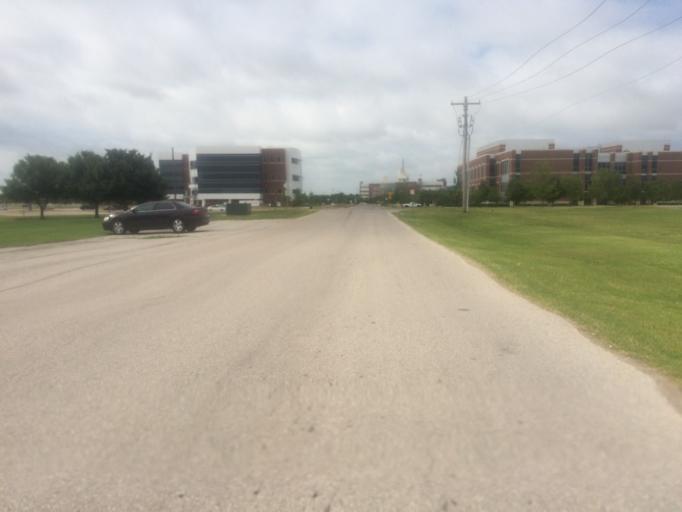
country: US
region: Oklahoma
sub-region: Cleveland County
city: Norman
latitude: 35.1879
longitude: -97.4396
